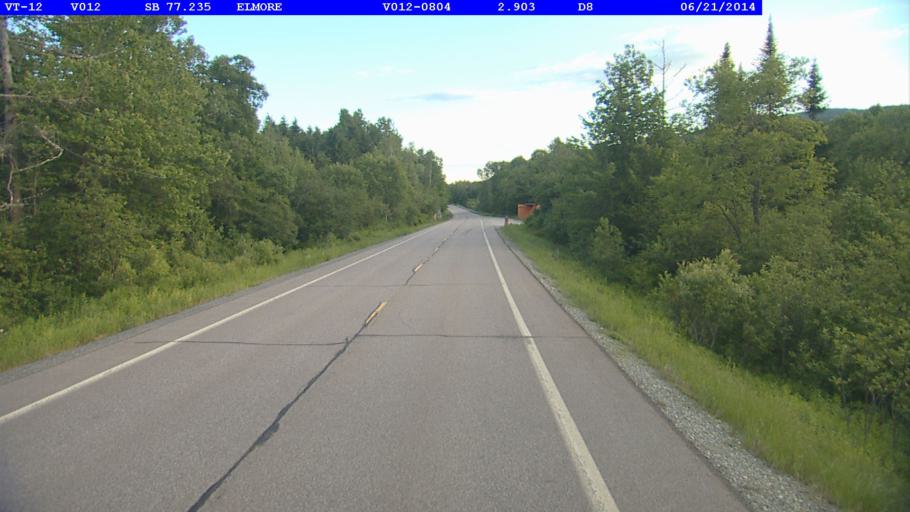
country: US
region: Vermont
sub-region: Lamoille County
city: Morrisville
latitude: 44.4882
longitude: -72.5239
